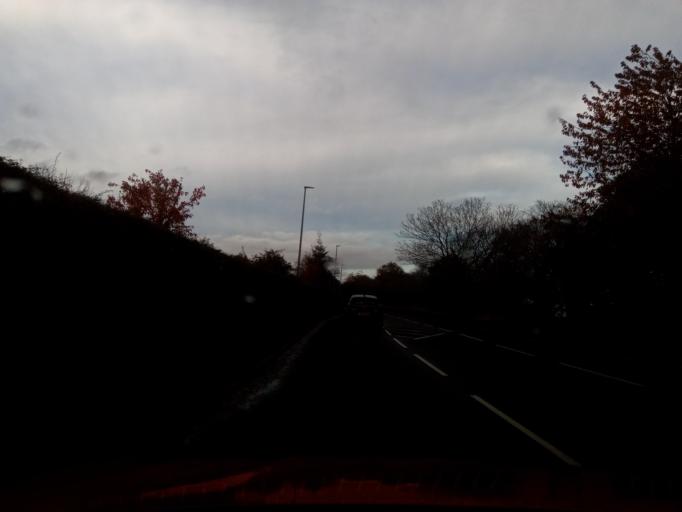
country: GB
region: Scotland
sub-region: The Scottish Borders
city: Kelso
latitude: 55.6064
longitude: -2.4144
